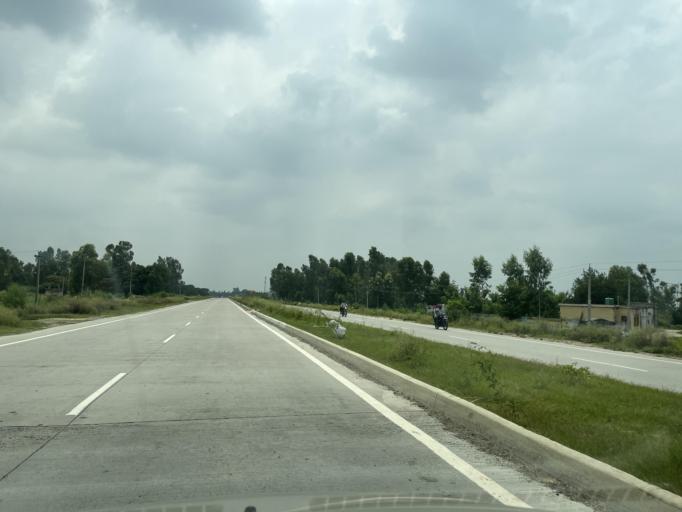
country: IN
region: Uttar Pradesh
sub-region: Bijnor
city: Najibabad
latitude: 29.5572
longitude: 78.3390
